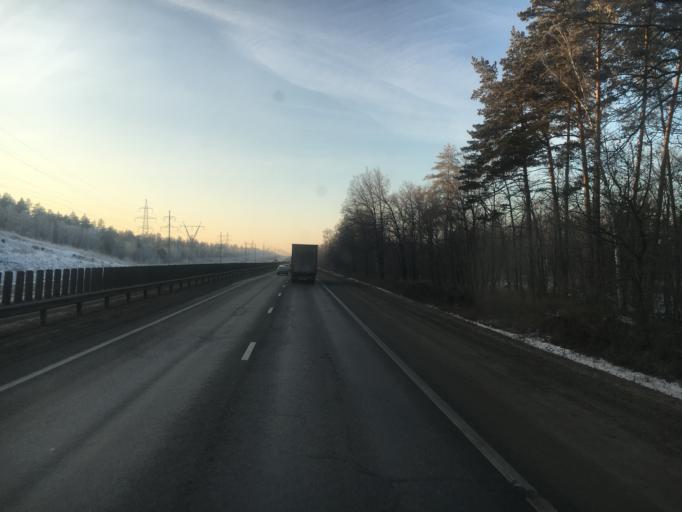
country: RU
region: Samara
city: Pribrezhnyy
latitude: 53.5145
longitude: 49.8916
